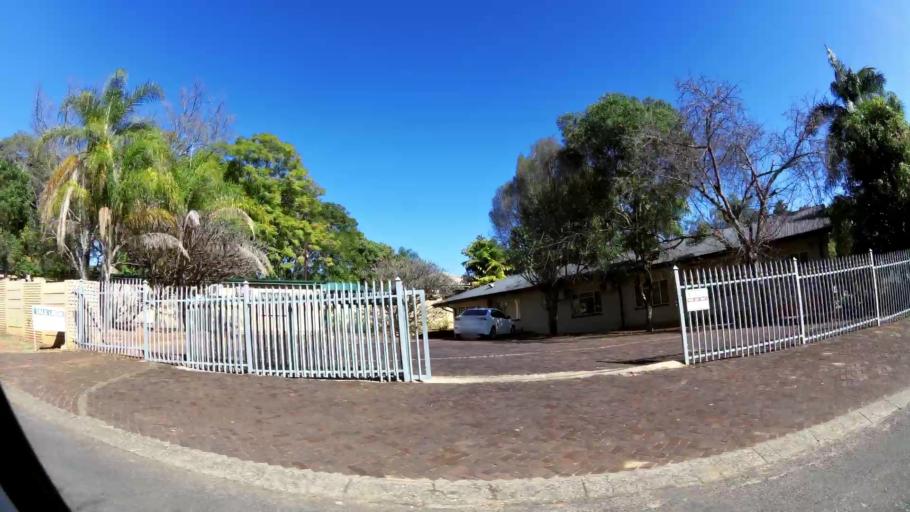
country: ZA
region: Limpopo
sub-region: Mopani District Municipality
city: Tzaneen
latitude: -23.8287
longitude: 30.1568
